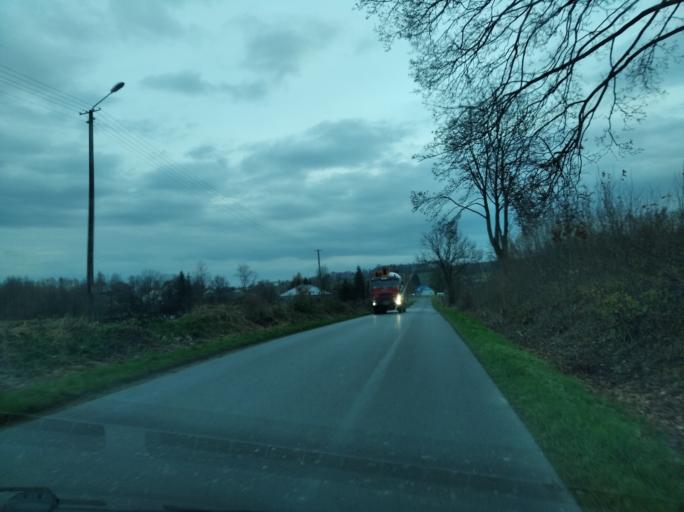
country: PL
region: Subcarpathian Voivodeship
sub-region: Powiat ropczycko-sedziszowski
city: Iwierzyce
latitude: 50.0381
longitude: 21.7460
